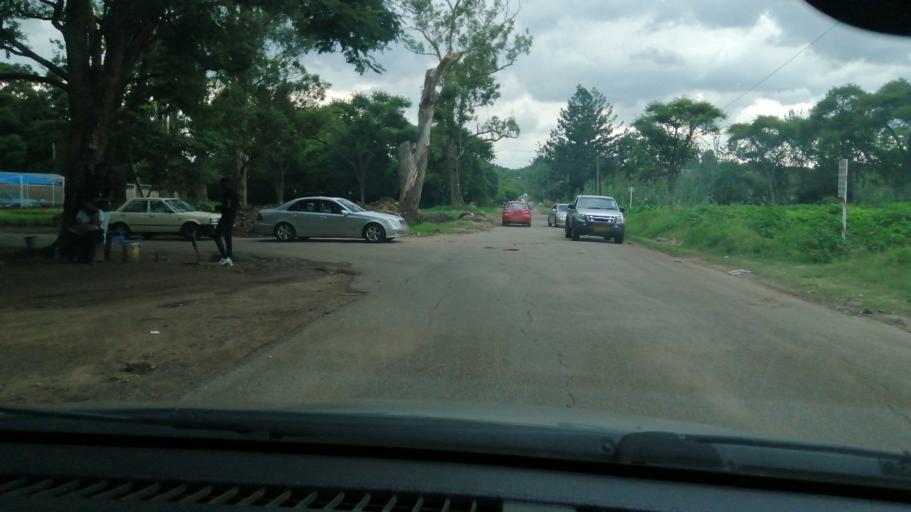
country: ZW
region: Harare
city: Harare
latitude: -17.7990
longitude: 31.0388
